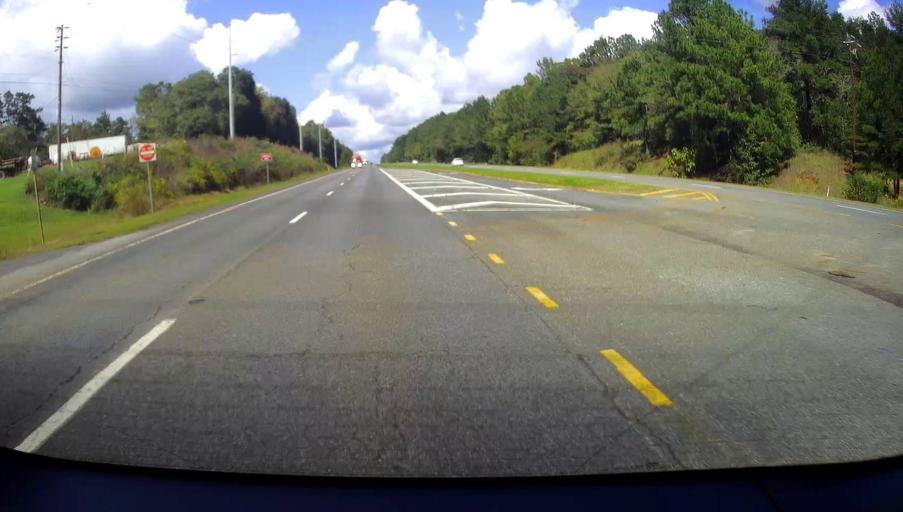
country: US
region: Georgia
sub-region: Jones County
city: Gray
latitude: 32.9508
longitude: -83.5799
